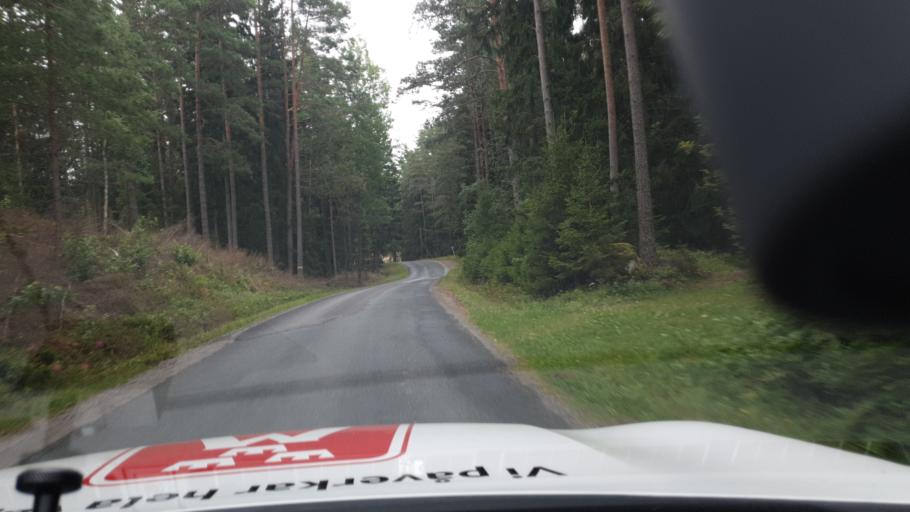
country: SE
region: Soedermanland
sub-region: Strangnas Kommun
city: Mariefred
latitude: 59.1730
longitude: 17.1763
